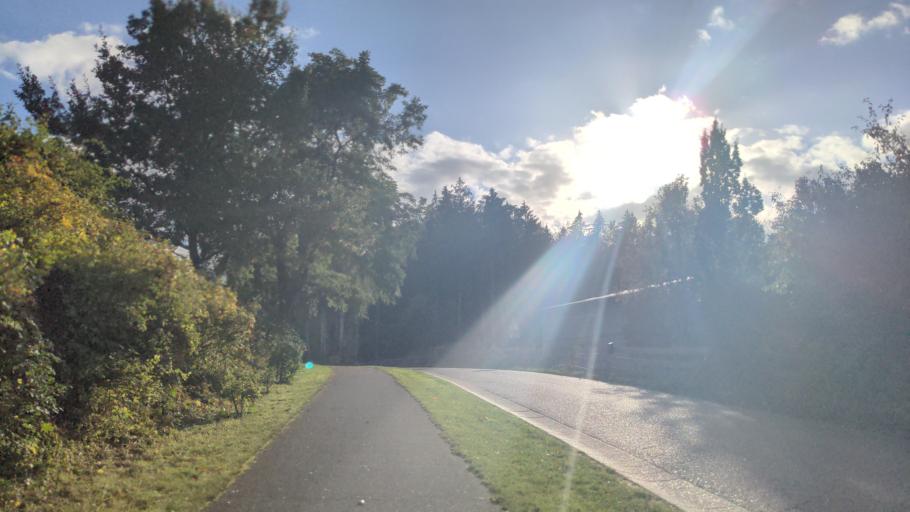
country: DE
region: Schleswig-Holstein
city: Bosau
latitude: 54.1195
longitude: 10.4442
